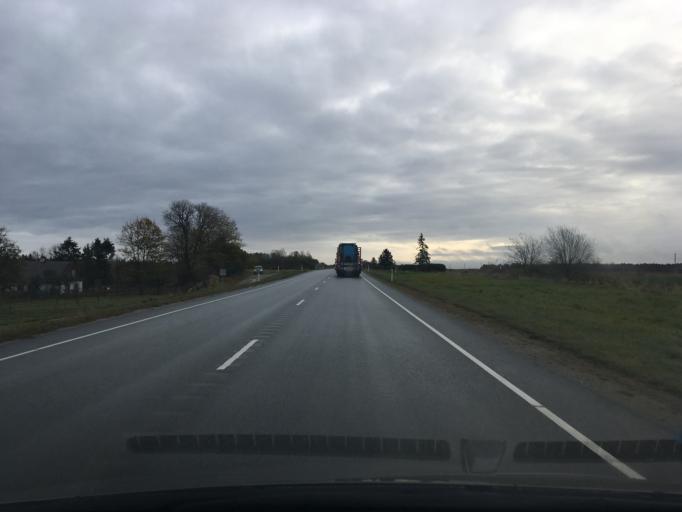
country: EE
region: Ida-Virumaa
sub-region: Aseri vald
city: Aseri
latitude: 59.4380
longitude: 26.8807
